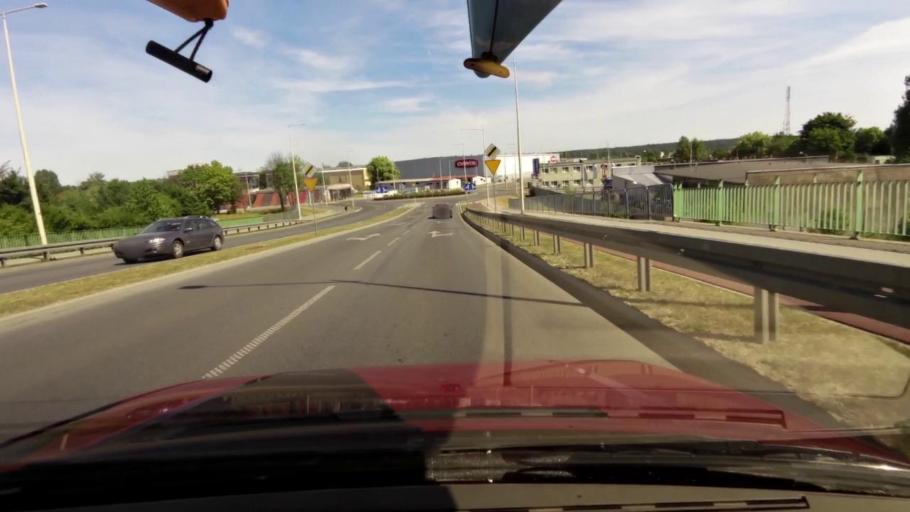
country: PL
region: Pomeranian Voivodeship
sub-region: Slupsk
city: Slupsk
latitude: 54.4549
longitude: 17.0118
